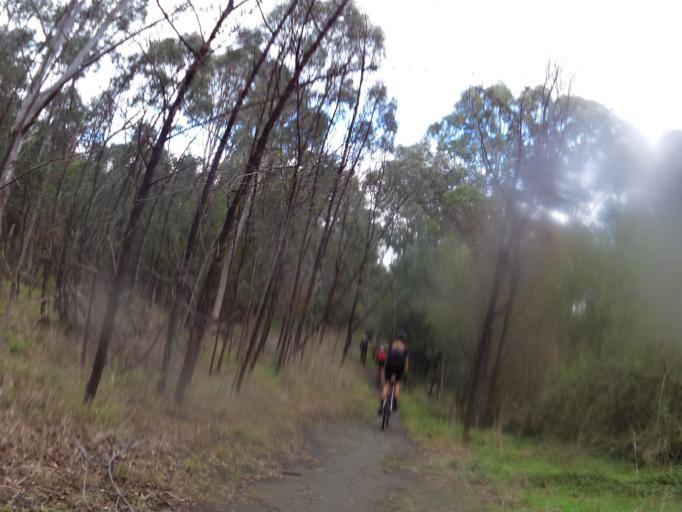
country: AU
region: Victoria
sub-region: Manningham
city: Bulleen
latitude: -37.7651
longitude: 145.0761
